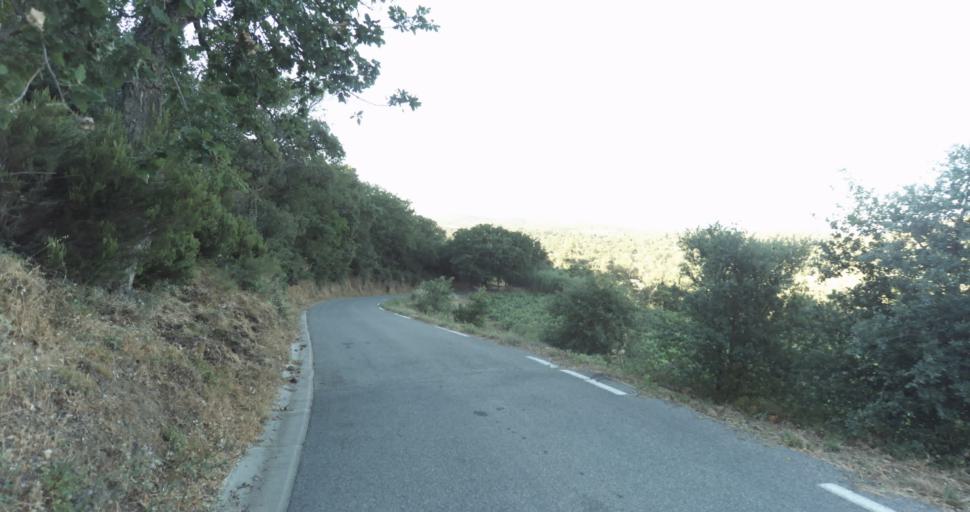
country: FR
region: Provence-Alpes-Cote d'Azur
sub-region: Departement du Var
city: Gassin
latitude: 43.2252
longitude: 6.5911
